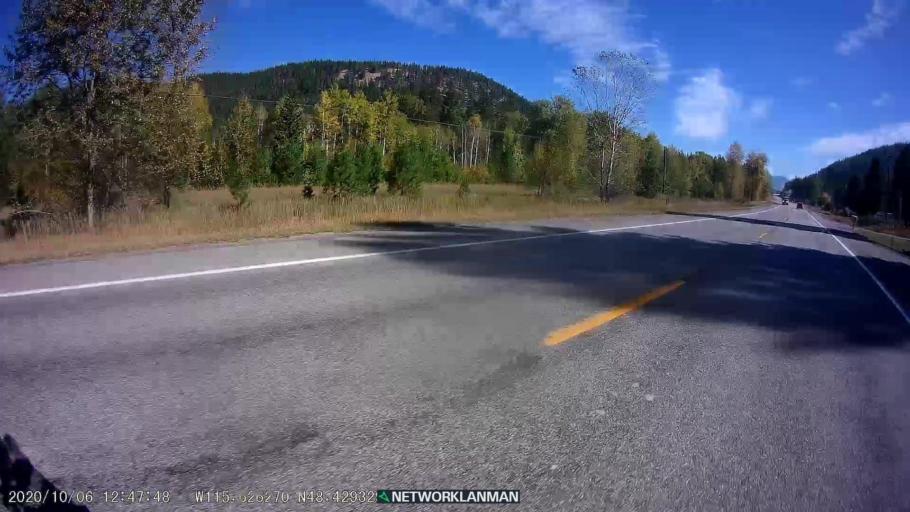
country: US
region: Montana
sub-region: Lincoln County
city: Libby
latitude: 48.4293
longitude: -115.6259
